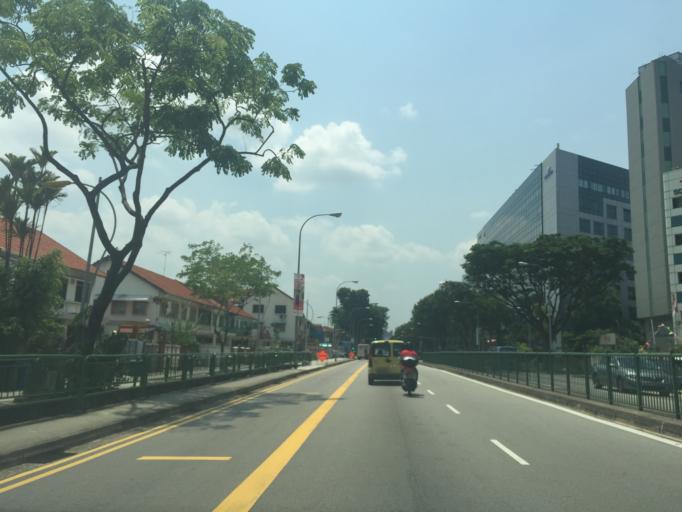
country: SG
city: Singapore
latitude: 1.3293
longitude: 103.8728
